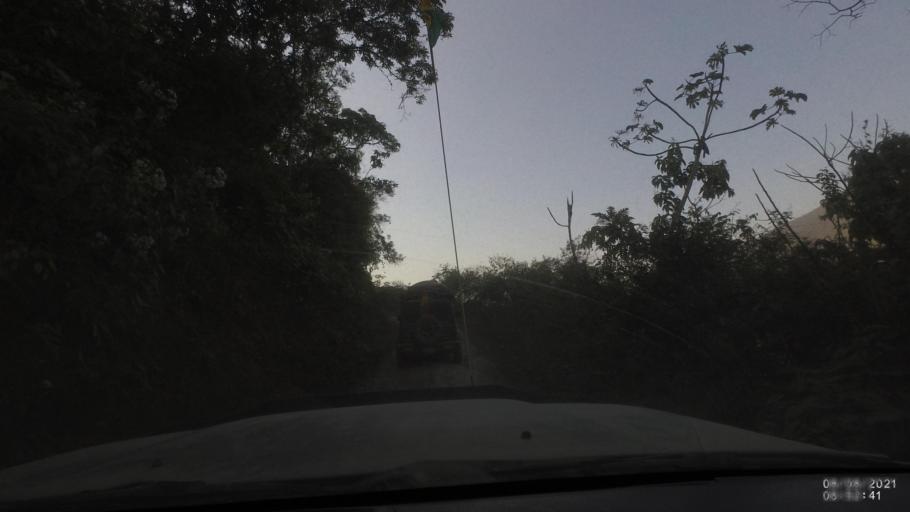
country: BO
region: La Paz
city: Quime
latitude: -16.5400
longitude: -66.7578
